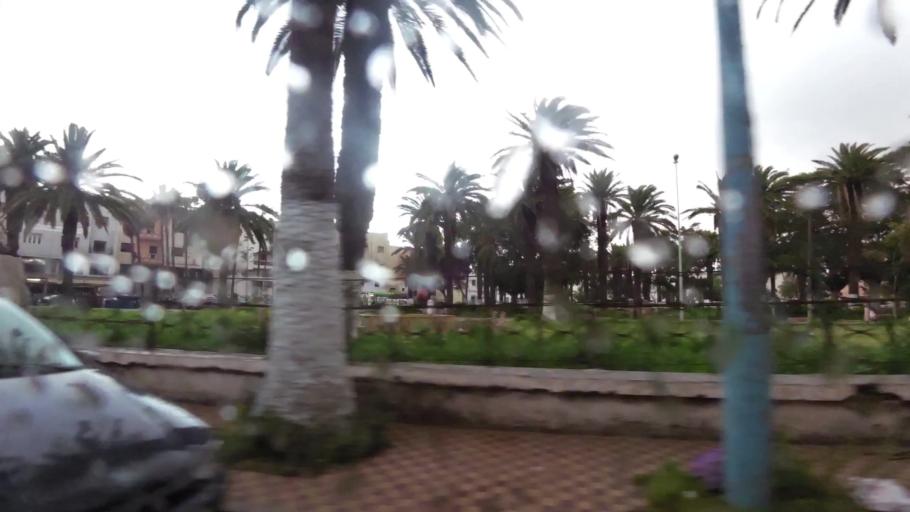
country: MA
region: Doukkala-Abda
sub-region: El-Jadida
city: El Jadida
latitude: 33.2574
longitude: -8.5061
